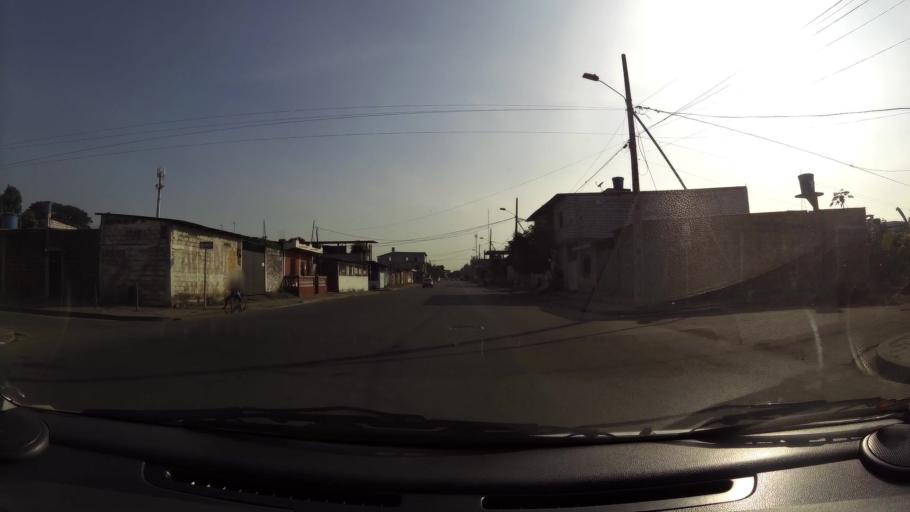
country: EC
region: Guayas
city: Eloy Alfaro
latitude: -2.1837
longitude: -79.8489
